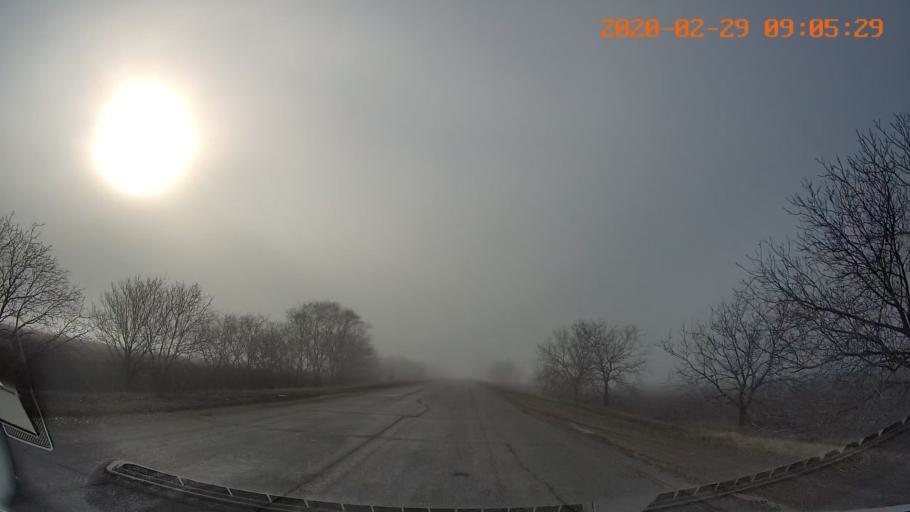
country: MD
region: Telenesti
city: Tiraspolul Nou
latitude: 46.8886
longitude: 29.7404
